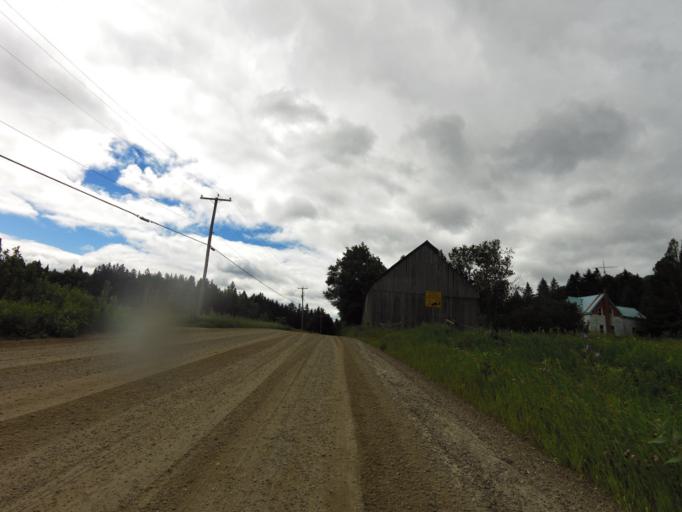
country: CA
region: Quebec
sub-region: Laurentides
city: Mont-Tremblant
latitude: 45.9532
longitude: -74.5935
